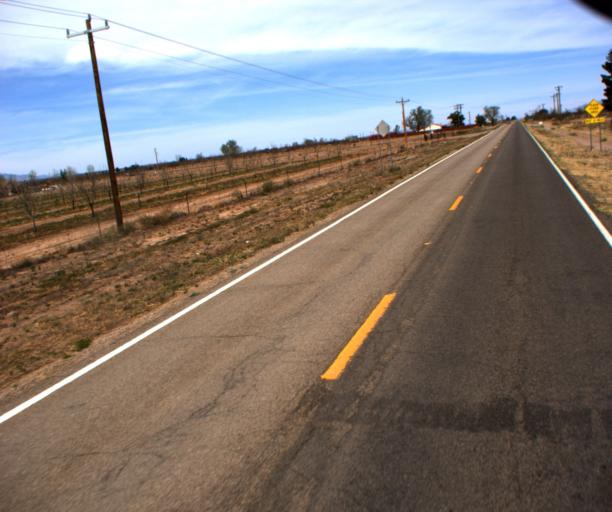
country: US
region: Arizona
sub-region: Cochise County
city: Bisbee
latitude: 31.7052
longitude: -109.6872
